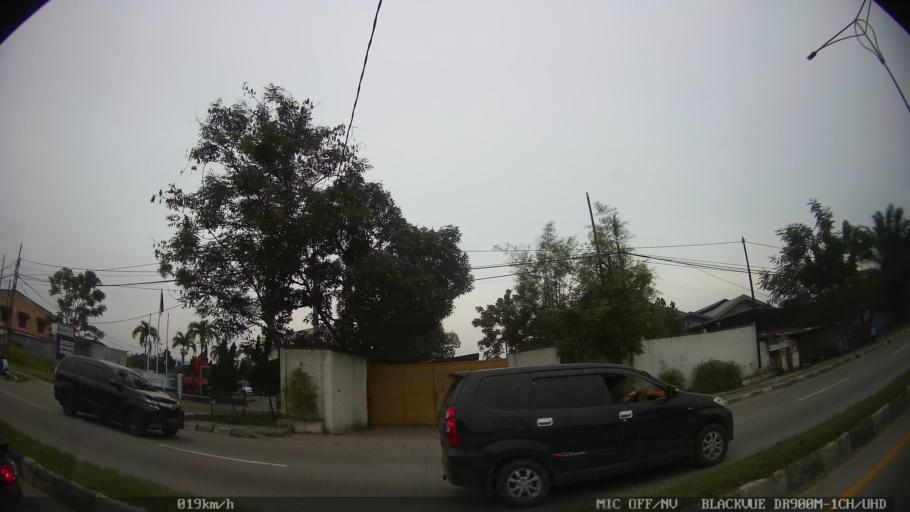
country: ID
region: North Sumatra
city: Deli Tua
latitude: 3.5323
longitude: 98.7308
